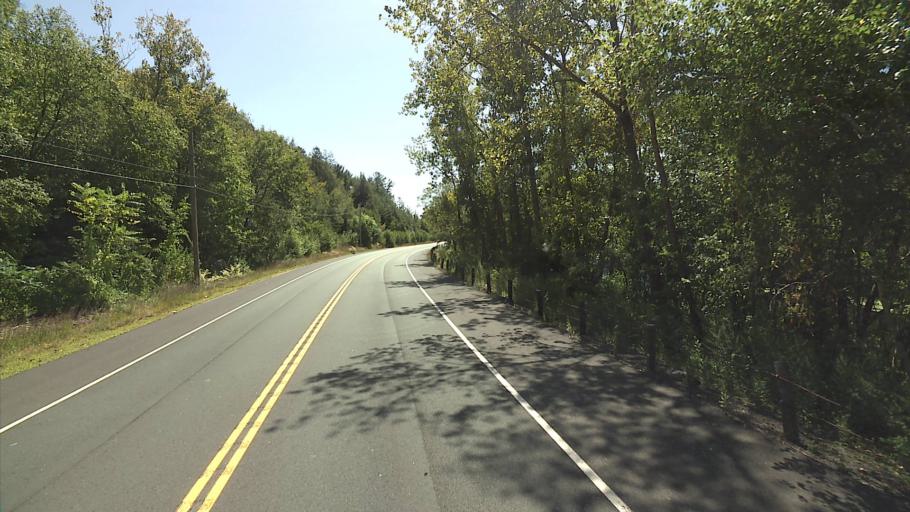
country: US
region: Connecticut
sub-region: Litchfield County
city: Oakville
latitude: 41.6044
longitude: -73.0585
